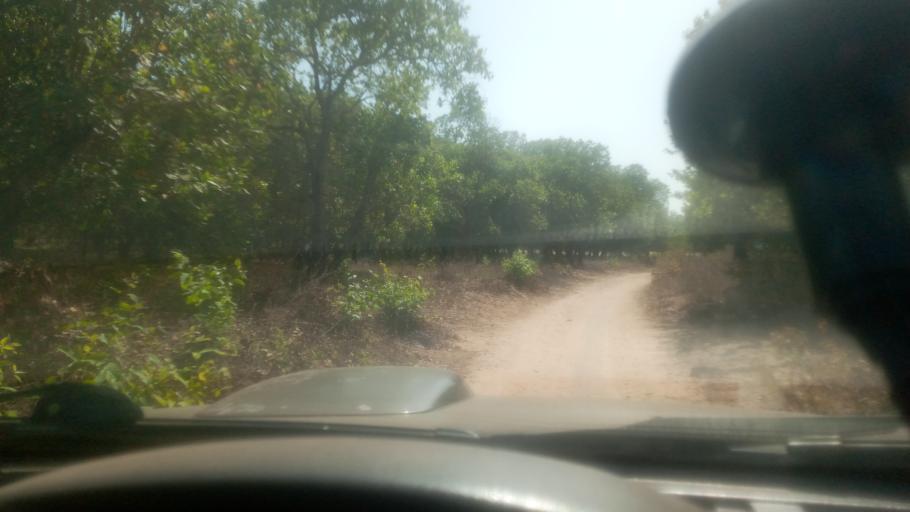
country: GW
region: Oio
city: Farim
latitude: 12.4528
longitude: -15.4207
